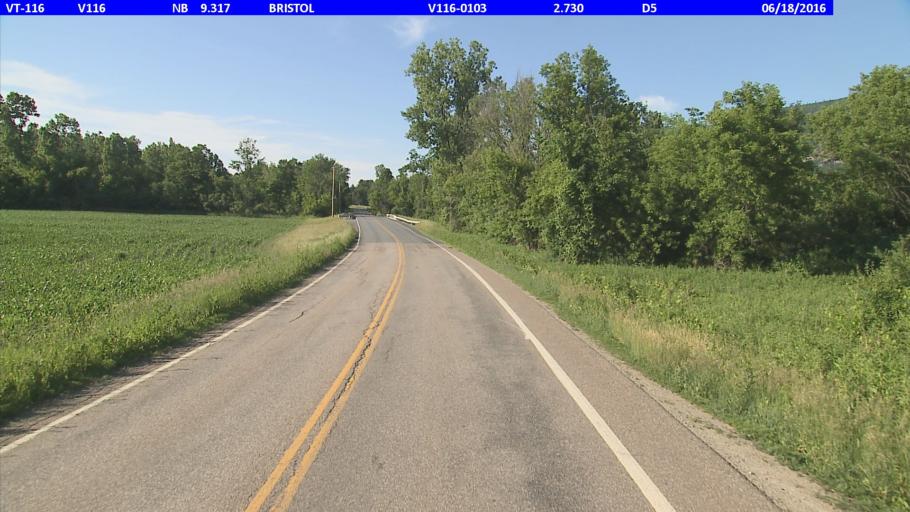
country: US
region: Vermont
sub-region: Addison County
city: Bristol
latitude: 44.0925
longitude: -73.0911
